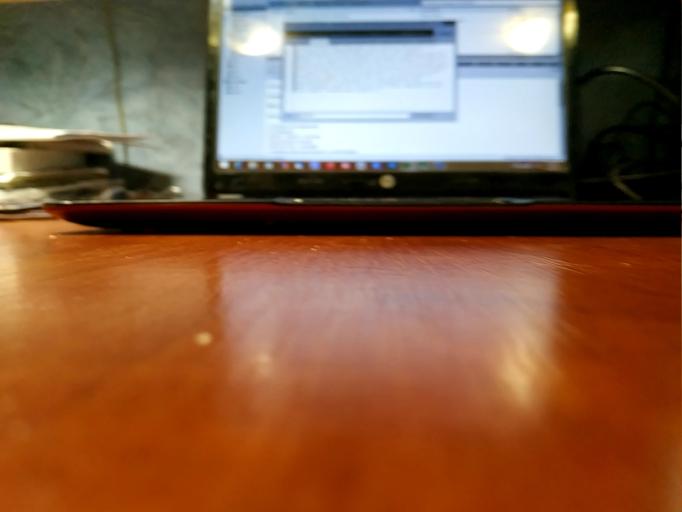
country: RU
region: Tverskaya
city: Sandovo
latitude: 58.5763
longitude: 36.4141
